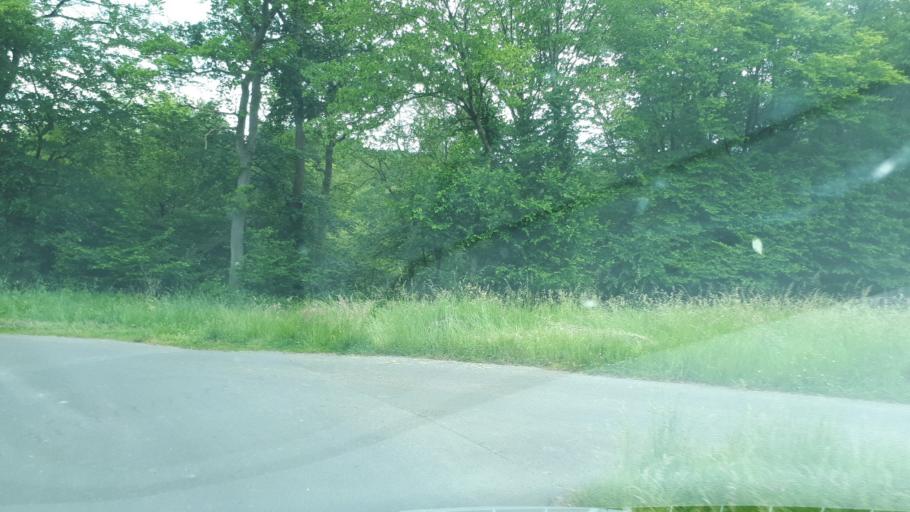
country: DE
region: Rheinland-Pfalz
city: Greimersburg
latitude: 50.1975
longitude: 7.1216
